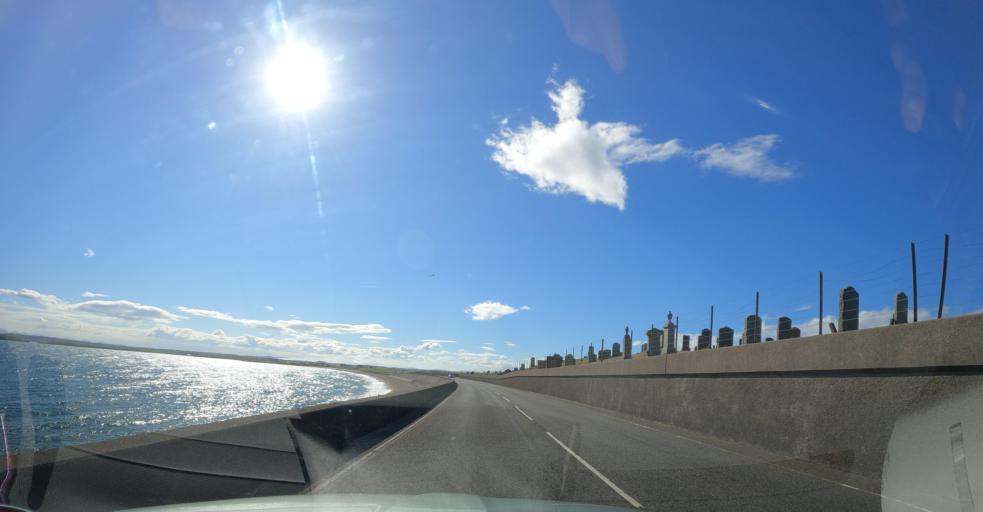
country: GB
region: Scotland
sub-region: Eilean Siar
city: Stornoway
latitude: 58.2059
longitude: -6.2888
